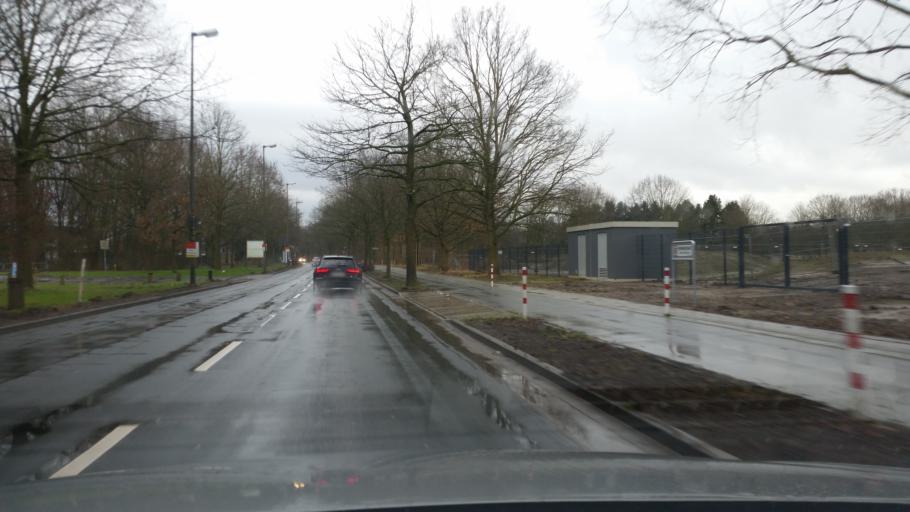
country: DE
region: Lower Saxony
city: Langenhagen
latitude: 52.4466
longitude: 9.7547
